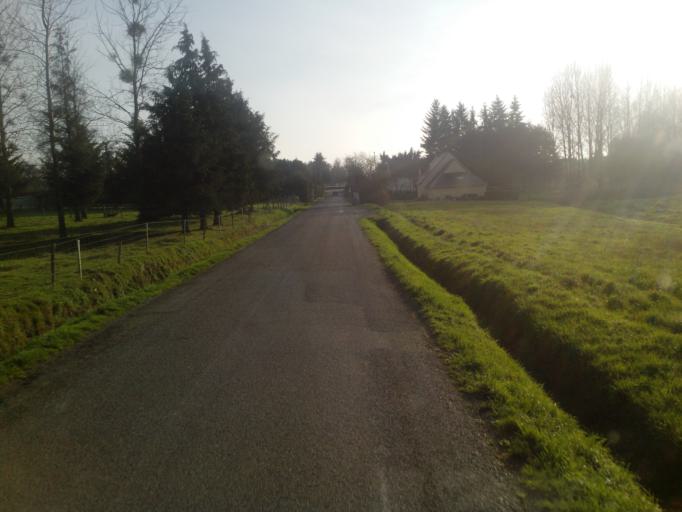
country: FR
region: Brittany
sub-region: Departement du Morbihan
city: Mauron
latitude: 48.0800
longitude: -2.2929
